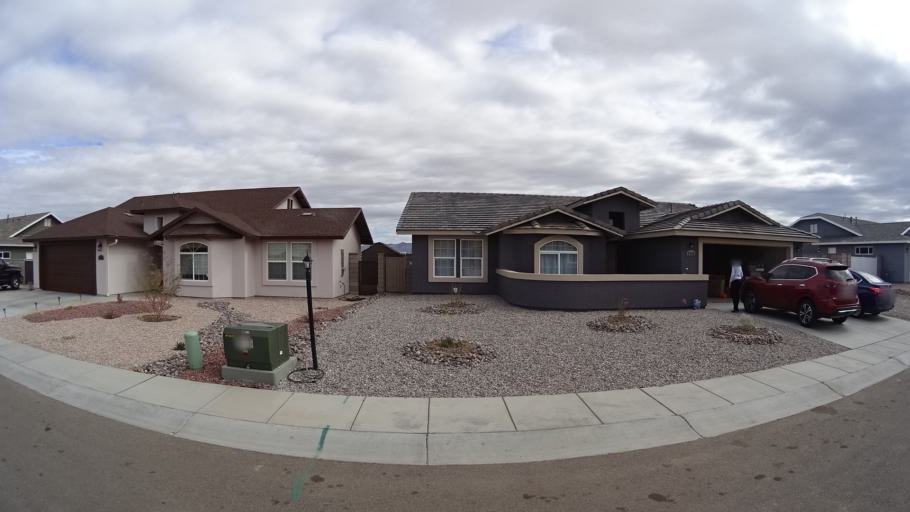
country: US
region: Arizona
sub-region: Mohave County
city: New Kingman-Butler
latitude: 35.2379
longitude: -113.9988
